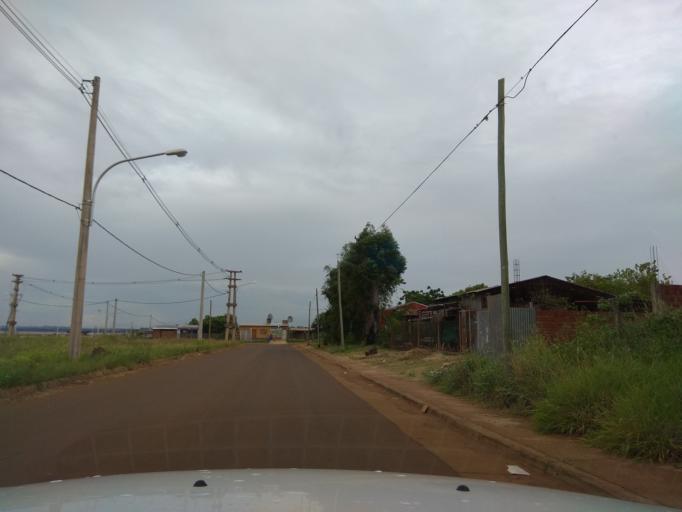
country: AR
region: Misiones
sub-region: Departamento de Capital
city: Posadas
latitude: -27.4274
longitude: -55.8725
